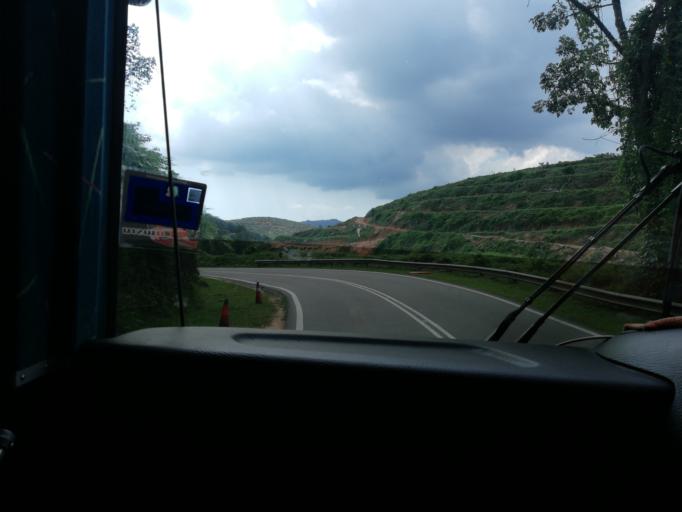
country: MY
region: Kedah
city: Kulim
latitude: 5.3088
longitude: 100.6120
